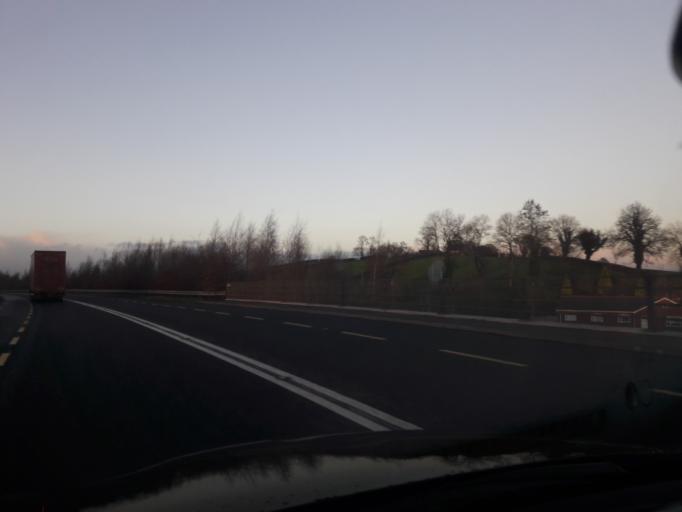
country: IE
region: Ulster
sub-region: County Monaghan
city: Monaghan
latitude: 54.2484
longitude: -6.9452
